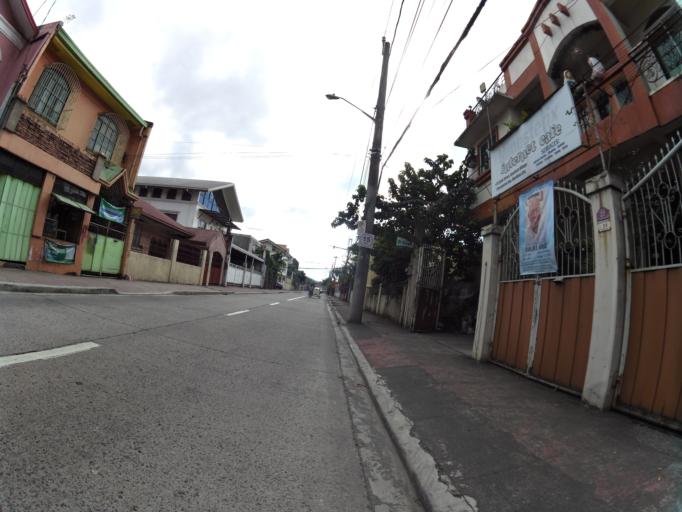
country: PH
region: Calabarzon
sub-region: Province of Rizal
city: Antipolo
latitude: 14.6420
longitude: 121.1068
